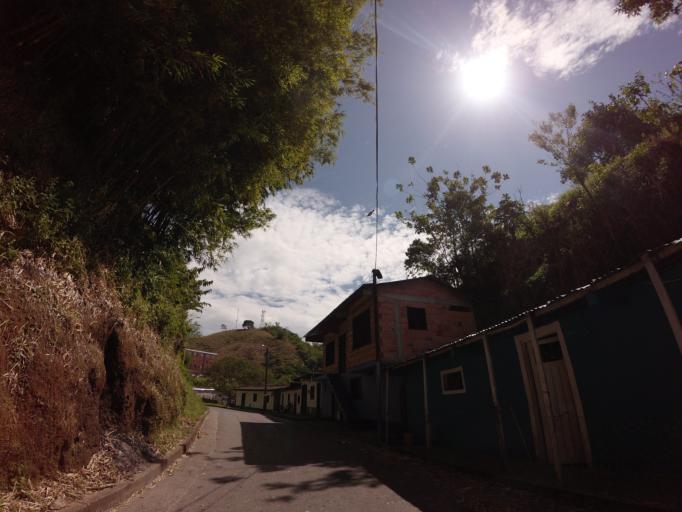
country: CO
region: Caldas
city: Norcasia
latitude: 5.5740
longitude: -74.8926
